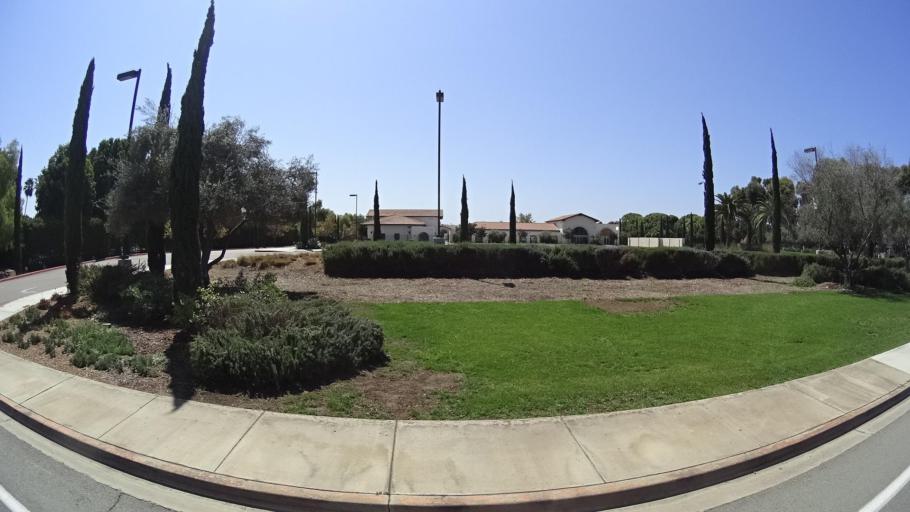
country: US
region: California
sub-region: San Diego County
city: Fairbanks Ranch
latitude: 32.9986
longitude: -117.1981
